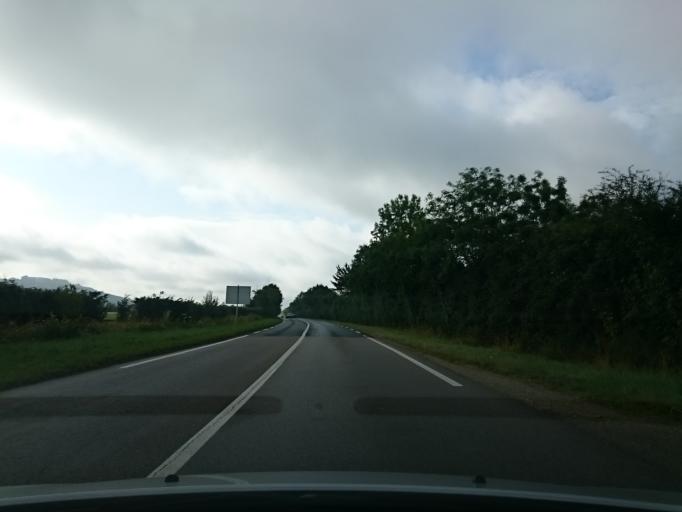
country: FR
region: Lower Normandy
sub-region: Departement du Calvados
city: Cambremer
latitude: 49.1388
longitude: -0.0075
